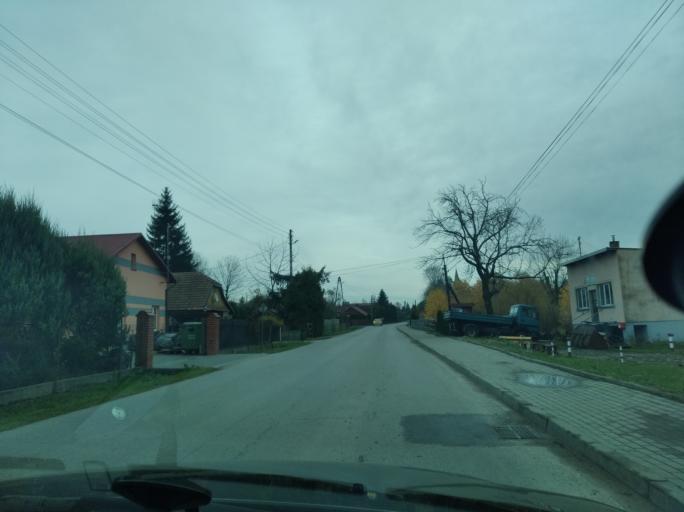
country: PL
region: Subcarpathian Voivodeship
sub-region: Powiat przeworski
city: Gac
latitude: 50.0269
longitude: 22.3510
